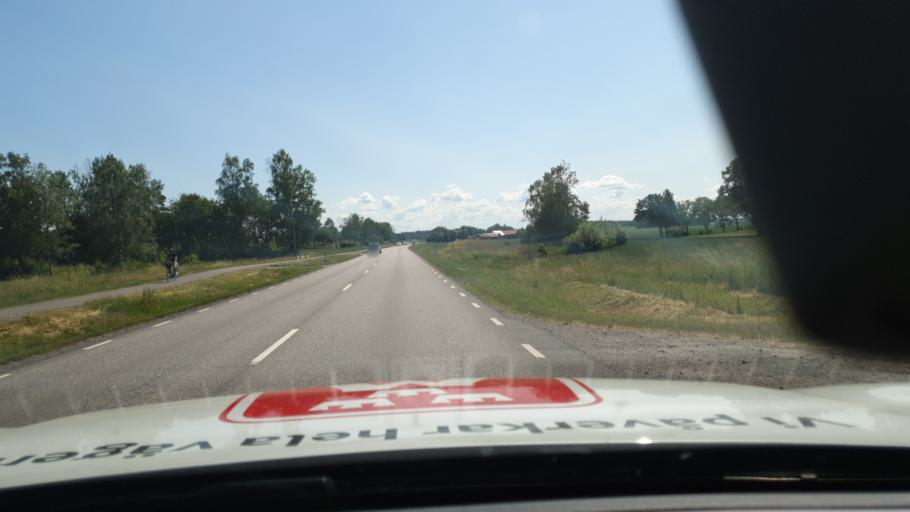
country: SE
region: Vaestra Goetaland
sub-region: Lidkopings Kommun
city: Lidkoping
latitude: 58.5510
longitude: 13.1153
